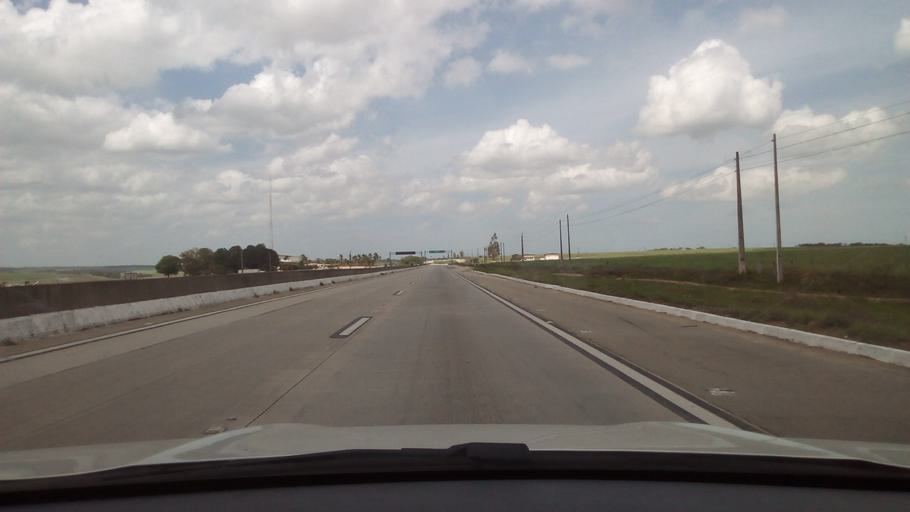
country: BR
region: Paraiba
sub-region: Mamanguape
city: Mamanguape
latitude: -6.7993
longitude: -35.1386
